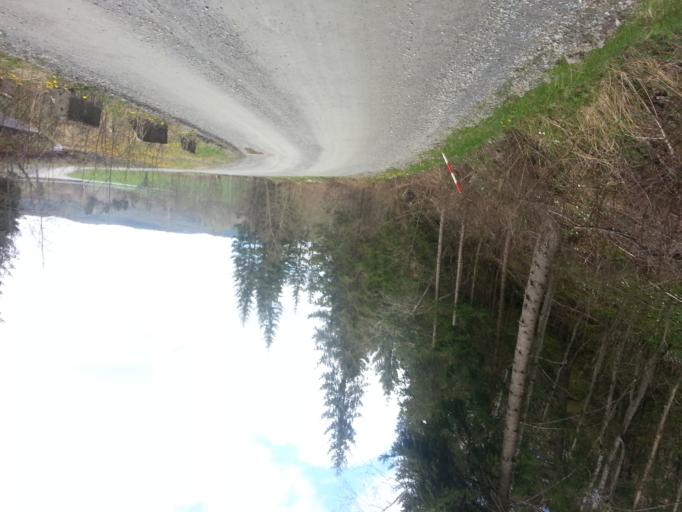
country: NO
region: Nord-Trondelag
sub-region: Levanger
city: Skogn
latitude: 63.6318
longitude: 11.2734
